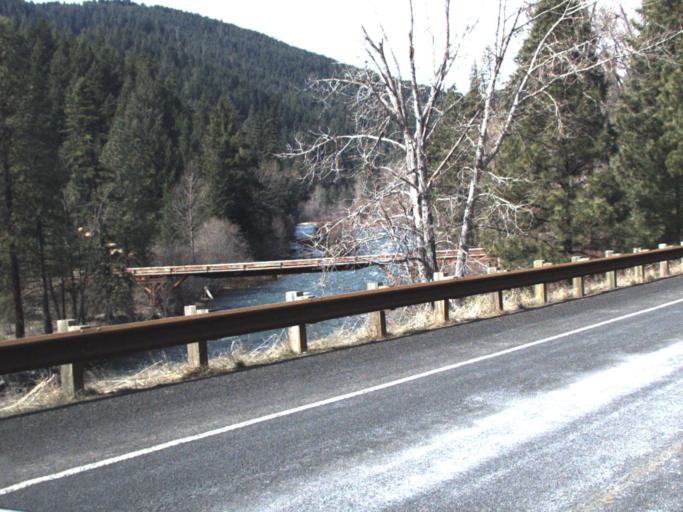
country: US
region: Washington
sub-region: Kittitas County
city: Cle Elum
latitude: 46.9062
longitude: -121.0234
